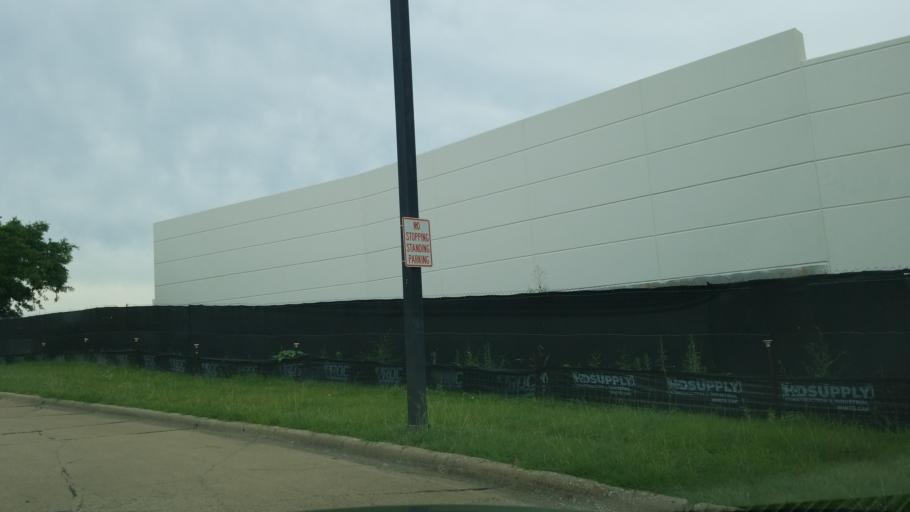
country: US
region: Texas
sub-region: Dallas County
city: Coppell
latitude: 32.8945
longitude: -96.9833
